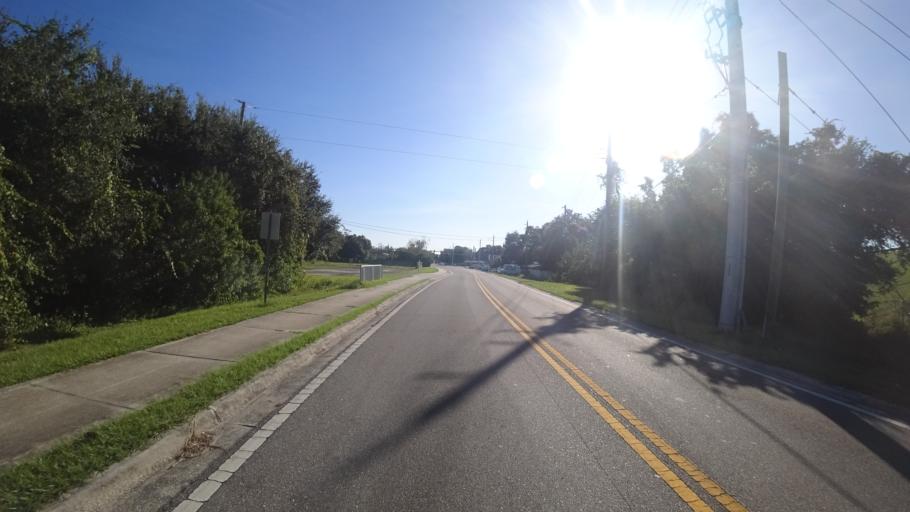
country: US
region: Florida
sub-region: Manatee County
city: Samoset
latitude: 27.4770
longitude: -82.5485
